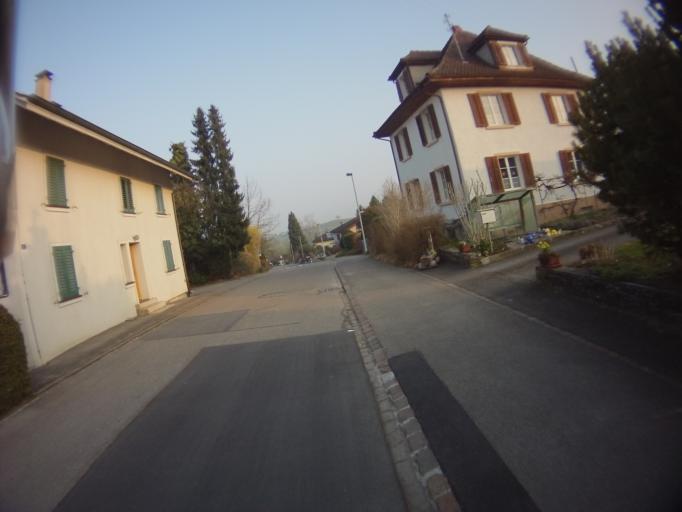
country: CH
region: Zurich
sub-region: Bezirk Affoltern
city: Obfelden
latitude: 47.2640
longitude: 8.4230
